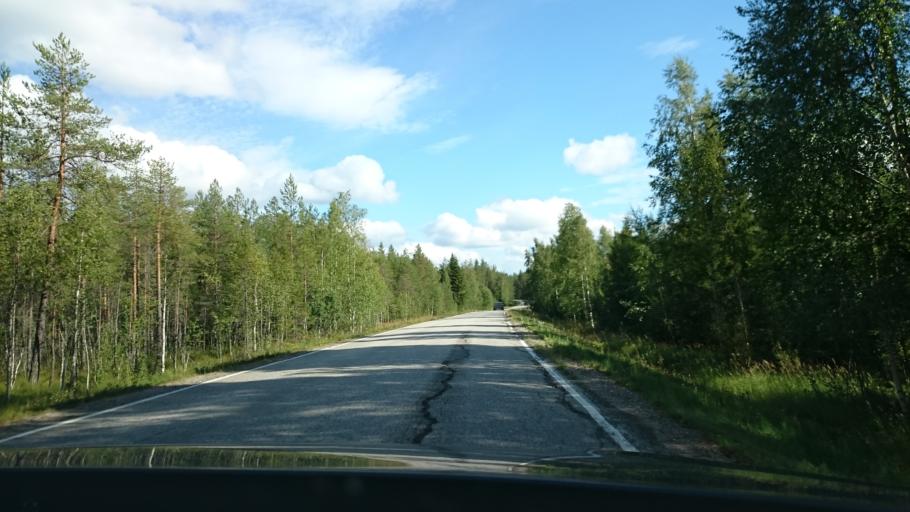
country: FI
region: Kainuu
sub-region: Kehys-Kainuu
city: Suomussalmi
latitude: 64.7549
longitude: 29.4141
